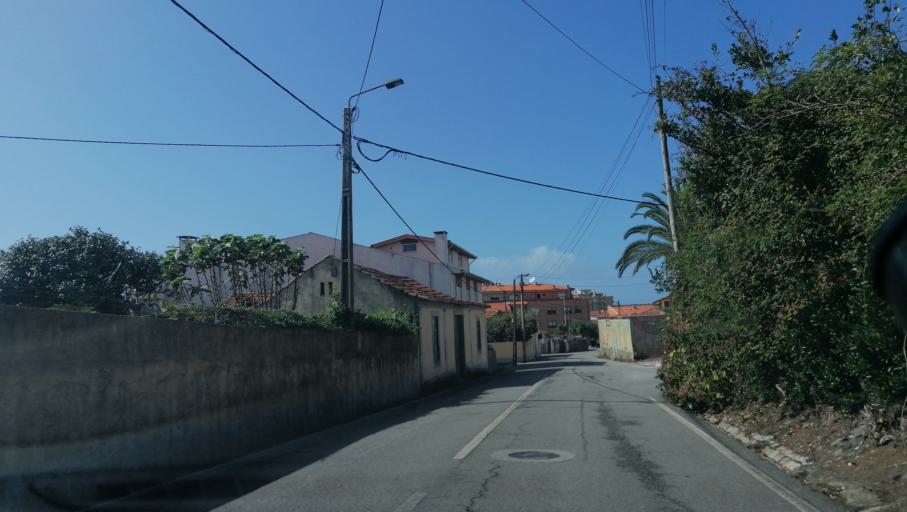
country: PT
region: Aveiro
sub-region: Espinho
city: Espinho
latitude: 41.0062
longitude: -8.6289
